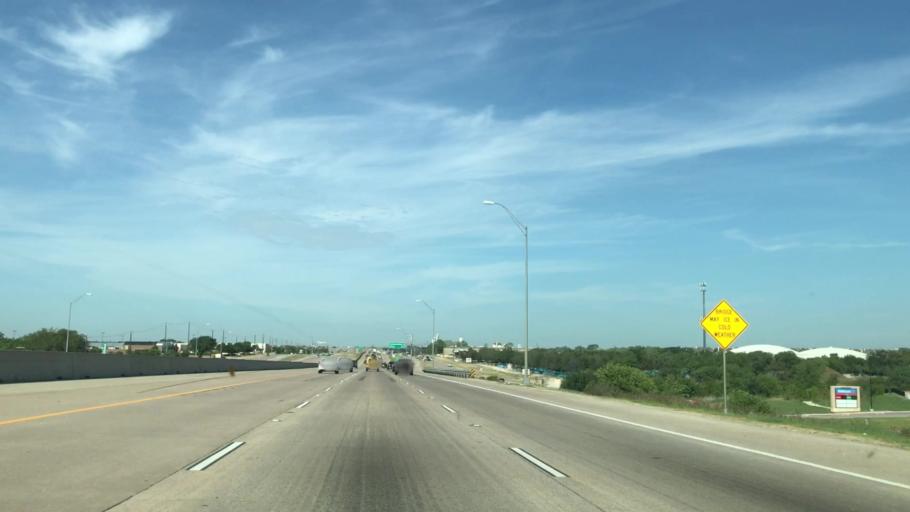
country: US
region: Texas
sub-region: Collin County
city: Allen
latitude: 33.1251
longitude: -96.7336
